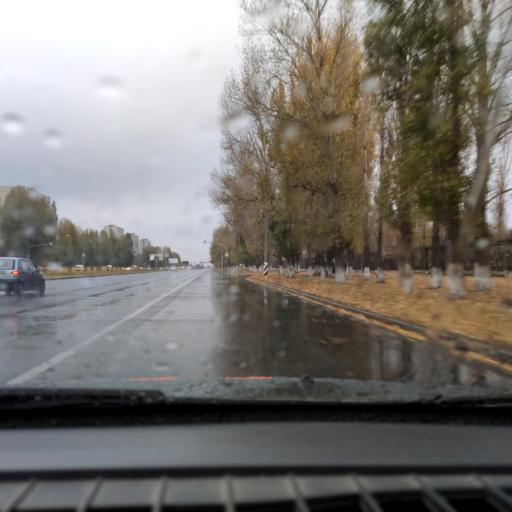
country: RU
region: Samara
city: Tol'yatti
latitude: 53.5131
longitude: 49.2773
